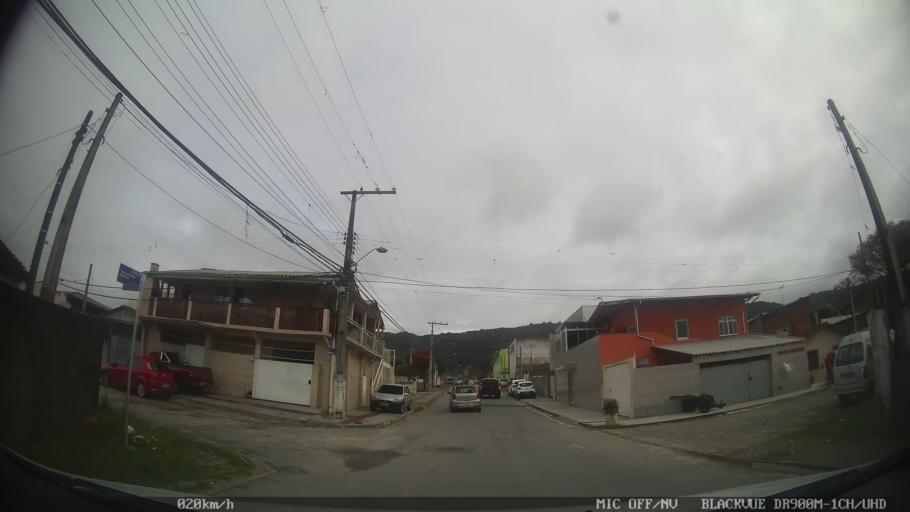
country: BR
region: Santa Catarina
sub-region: Biguacu
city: Biguacu
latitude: -27.5403
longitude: -48.6437
